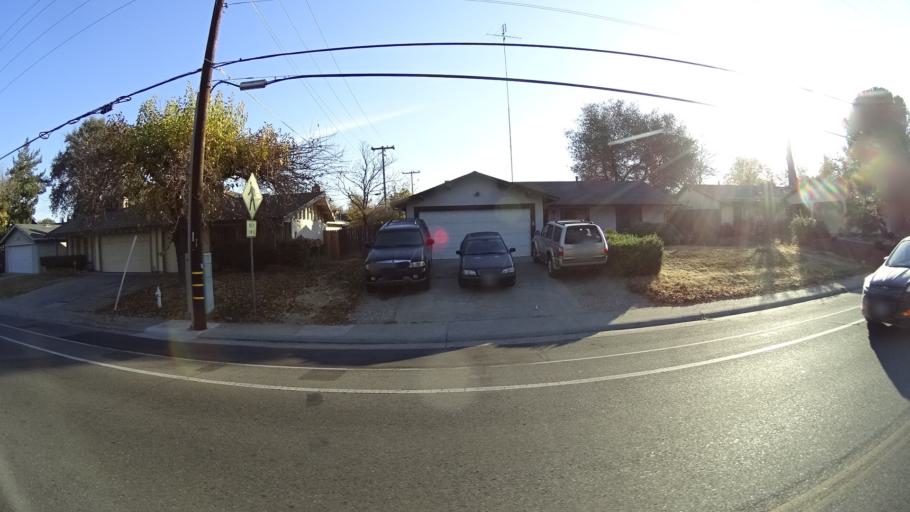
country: US
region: California
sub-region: Sacramento County
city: Antelope
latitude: 38.6953
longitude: -121.3087
